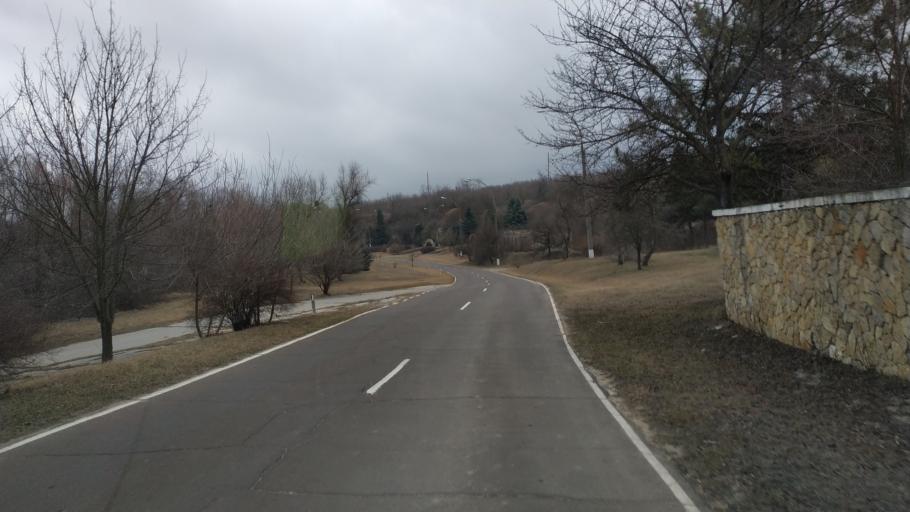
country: MD
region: Laloveni
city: Ialoveni
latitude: 46.9251
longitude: 28.8163
